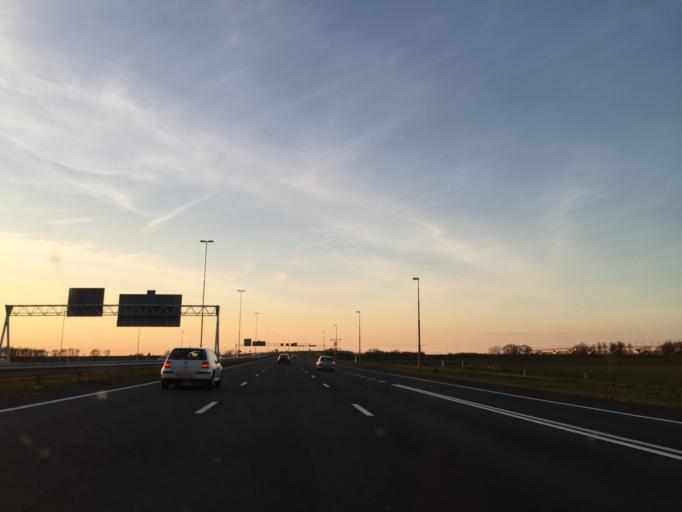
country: NL
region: South Holland
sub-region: Gemeente Strijen
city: Strijen
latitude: 51.7060
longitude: 4.6450
